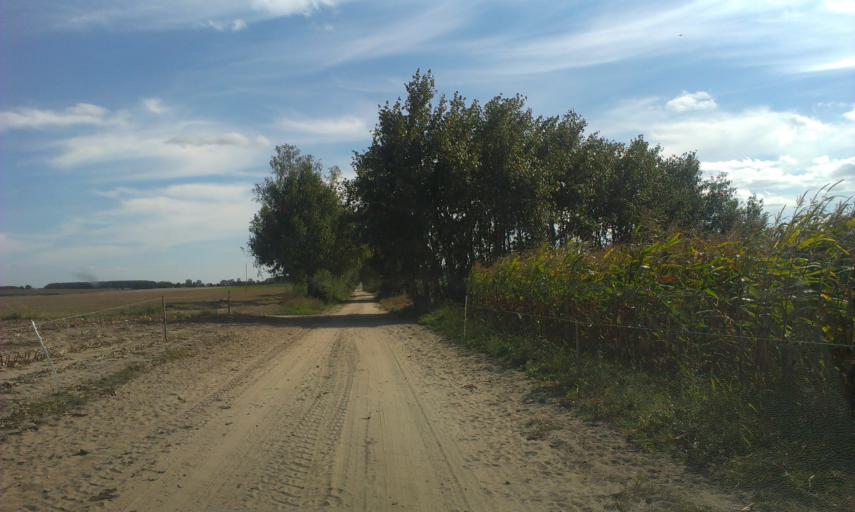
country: PL
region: Greater Poland Voivodeship
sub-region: Powiat pilski
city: Lobzenica
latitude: 53.2959
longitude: 17.1516
